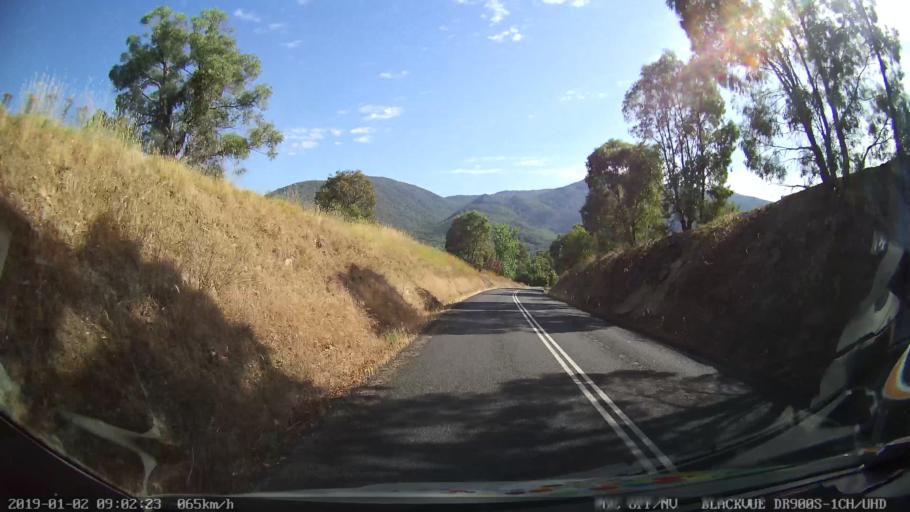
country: AU
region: New South Wales
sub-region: Tumut Shire
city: Tumut
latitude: -35.5733
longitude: 148.3121
